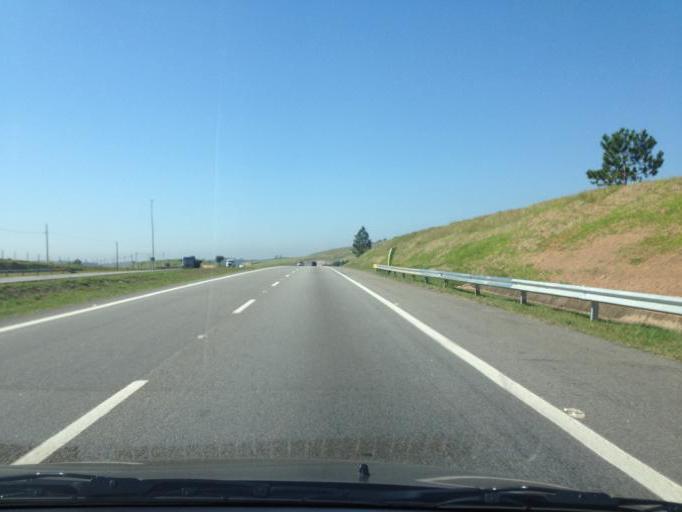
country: BR
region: Sao Paulo
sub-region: Guararema
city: Guararema
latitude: -23.3590
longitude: -46.0886
